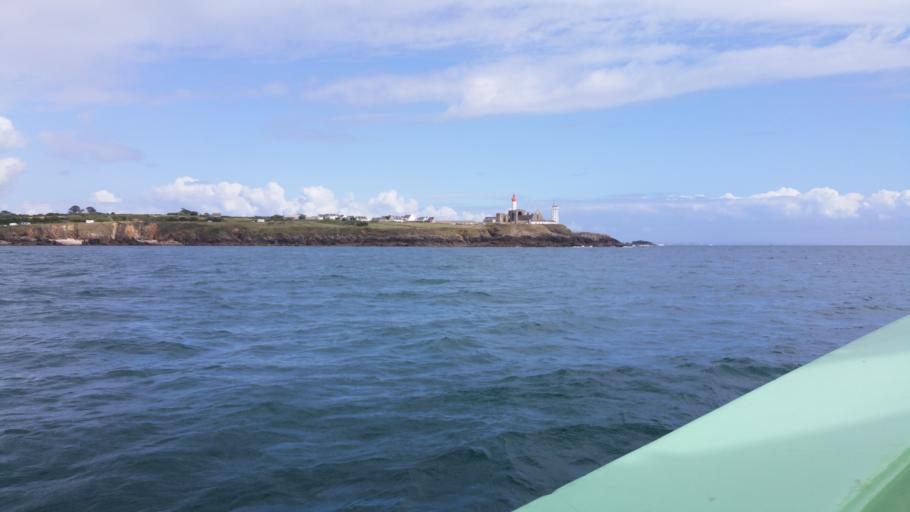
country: FR
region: Brittany
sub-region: Departement du Finistere
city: Le Conquet
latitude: 48.3334
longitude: -4.7820
